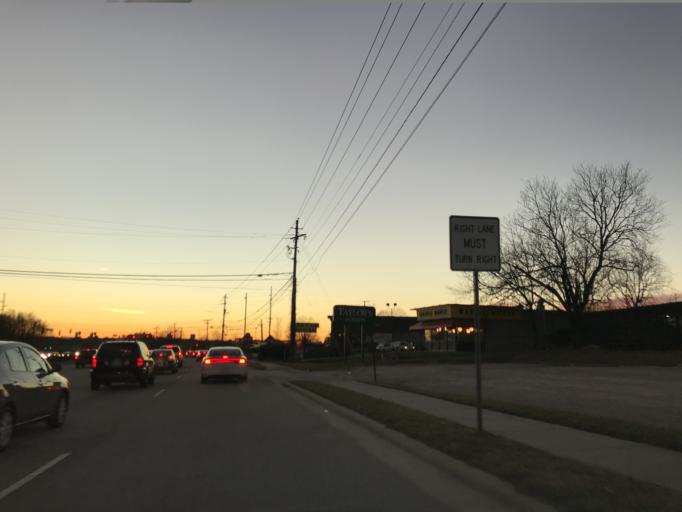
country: US
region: North Carolina
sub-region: Wake County
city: Raleigh
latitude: 35.7981
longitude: -78.5761
